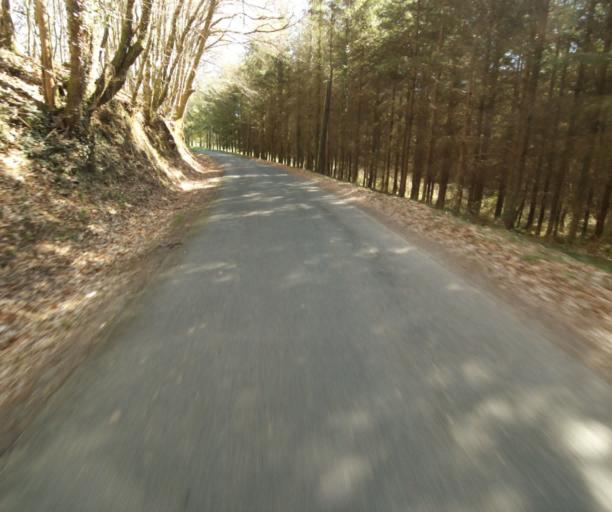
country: FR
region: Limousin
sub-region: Departement de la Correze
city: Chameyrat
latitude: 45.2762
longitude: 1.7003
